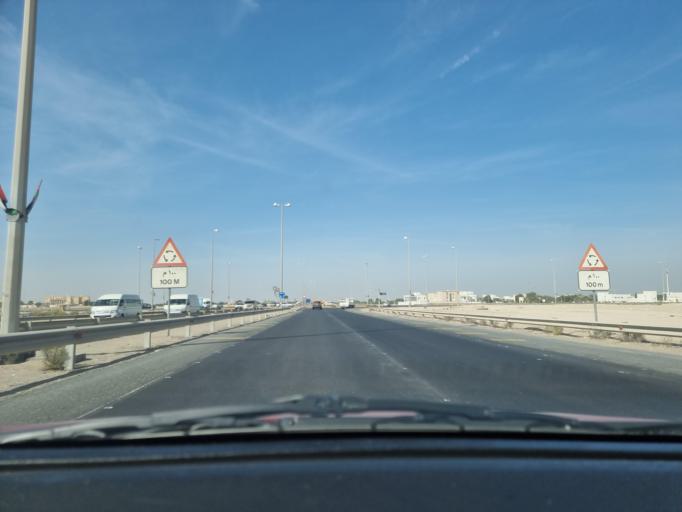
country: AE
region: Abu Dhabi
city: Abu Dhabi
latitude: 24.3637
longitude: 54.6624
